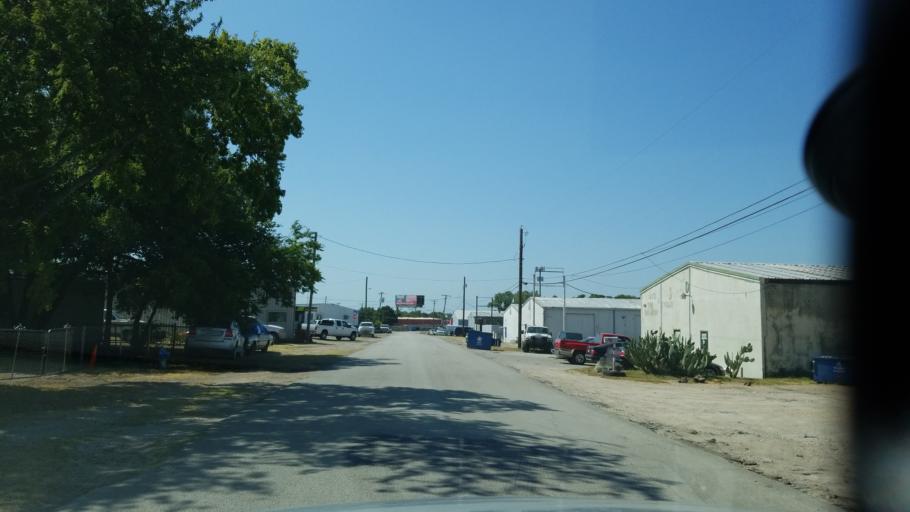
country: US
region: Texas
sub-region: Dallas County
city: Duncanville
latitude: 32.6378
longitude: -96.8990
